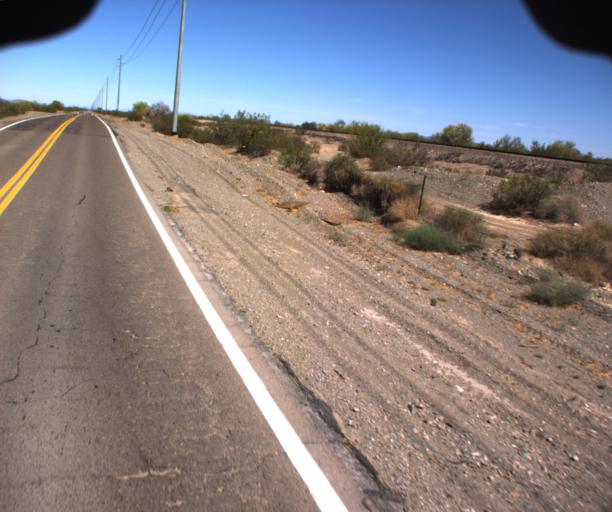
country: US
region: Arizona
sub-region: La Paz County
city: Salome
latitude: 33.7820
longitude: -113.8086
